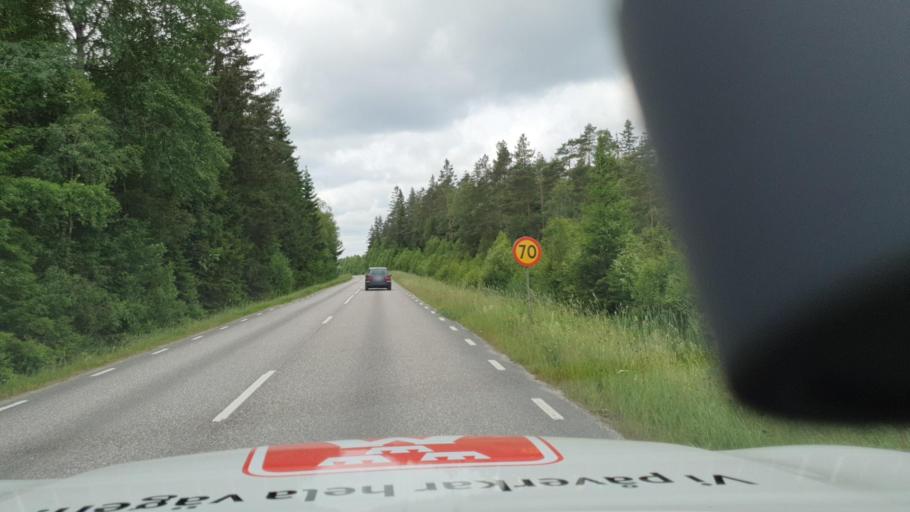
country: SE
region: Vaestra Goetaland
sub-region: Boras Kommun
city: Dalsjofors
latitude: 57.7498
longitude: 13.1505
